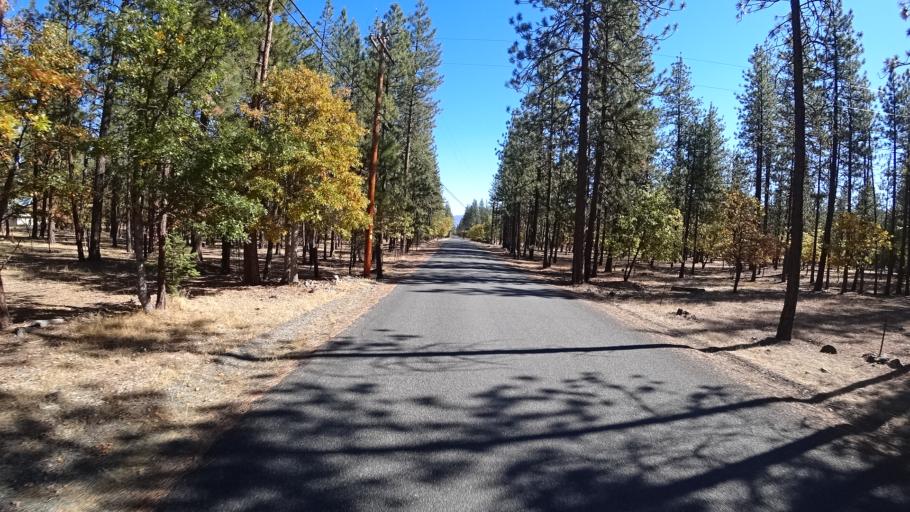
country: US
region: California
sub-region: Siskiyou County
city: Yreka
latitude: 41.5412
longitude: -122.9464
